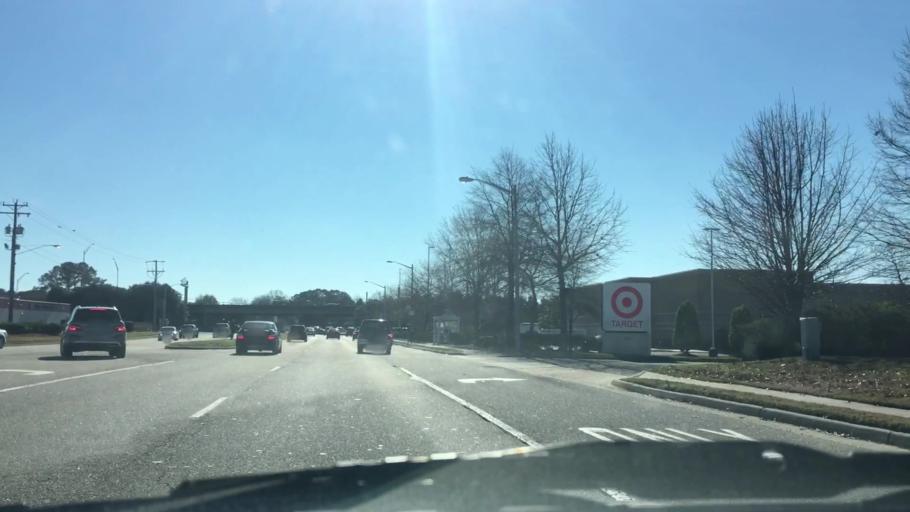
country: US
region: Virginia
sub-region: City of Virginia Beach
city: Virginia Beach
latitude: 36.8477
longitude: -76.0215
